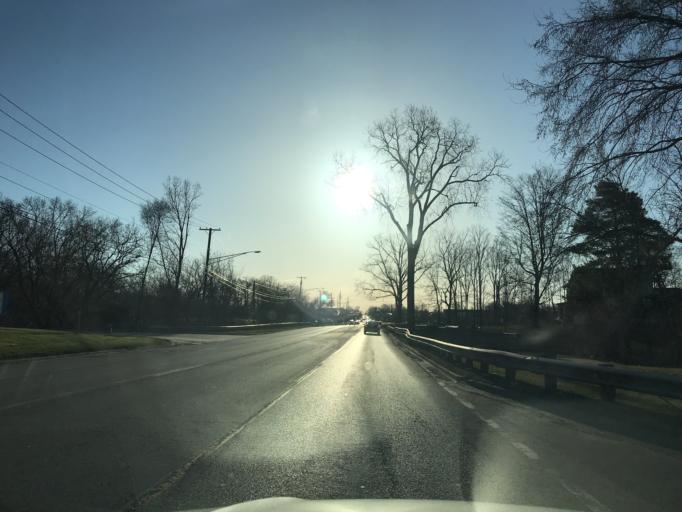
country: US
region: Michigan
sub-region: Oakland County
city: Wixom
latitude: 42.5241
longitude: -83.5431
